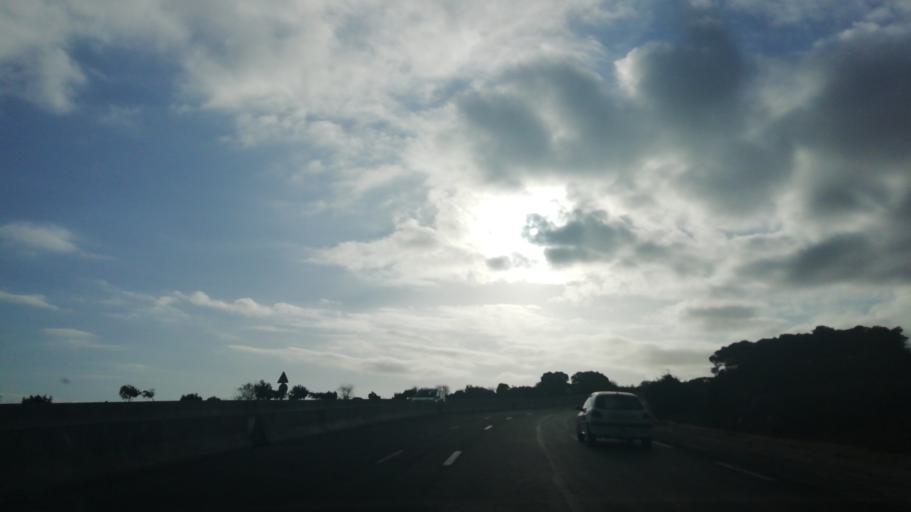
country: DZ
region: Mostaganem
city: Mostaganem
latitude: 36.1098
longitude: 0.2625
